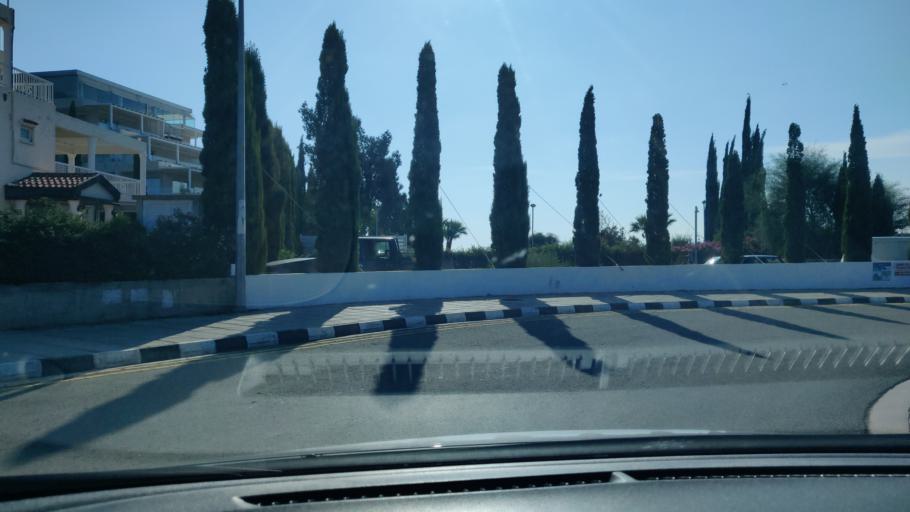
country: CY
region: Ammochostos
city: Protaras
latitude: 34.9855
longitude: 34.0670
